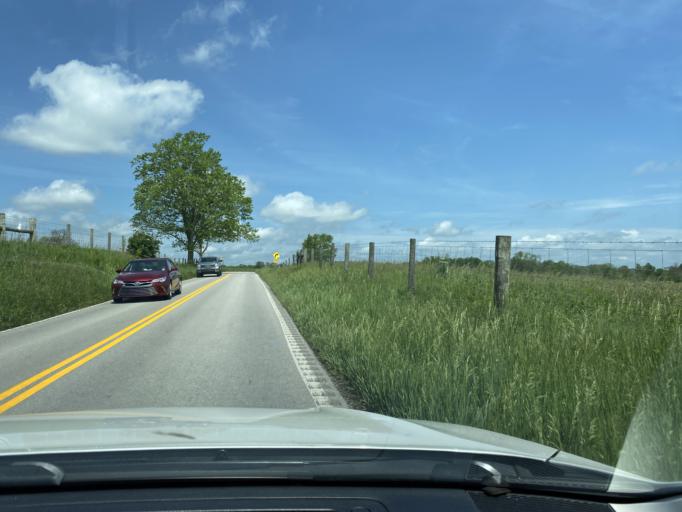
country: US
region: Kentucky
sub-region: Scott County
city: Georgetown
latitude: 38.2452
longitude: -84.5856
